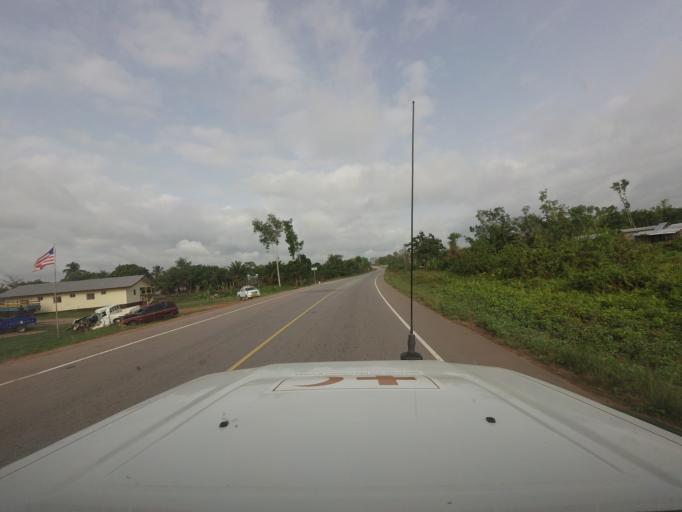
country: LR
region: Bong
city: Gbarnga
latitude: 7.0018
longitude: -9.2914
